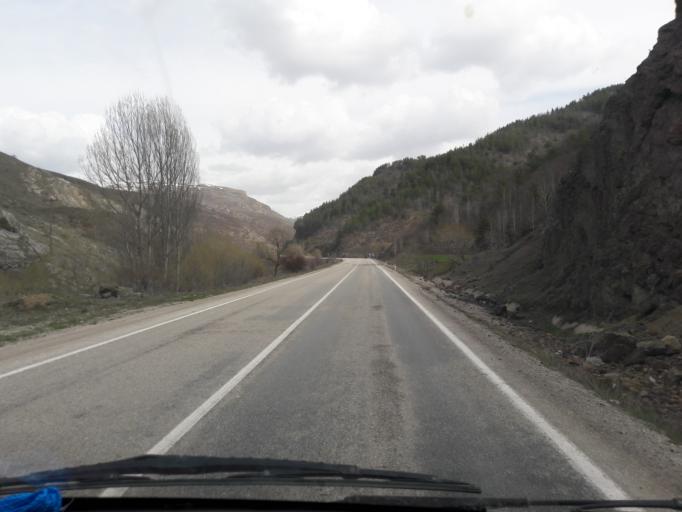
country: TR
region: Gumushane
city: Gumushkhane
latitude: 40.2919
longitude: 39.4798
